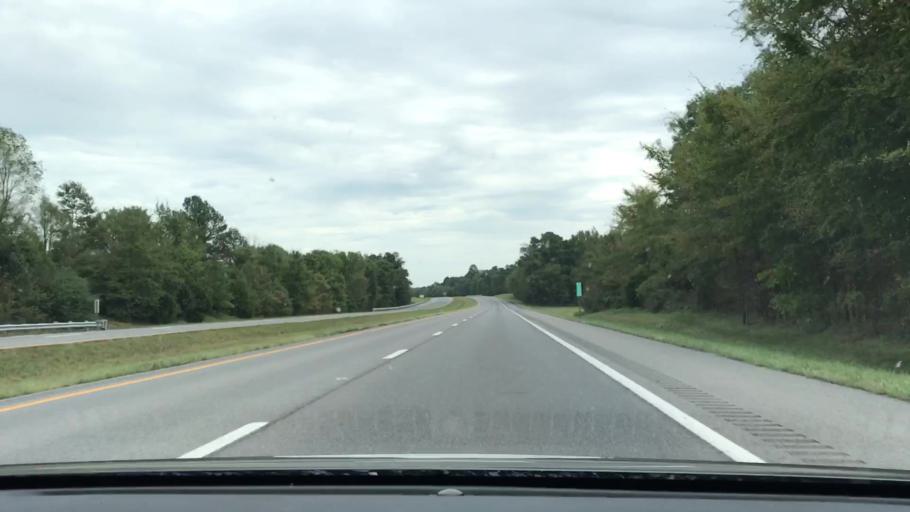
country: US
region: Kentucky
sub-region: Graves County
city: Mayfield
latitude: 36.7792
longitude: -88.5688
